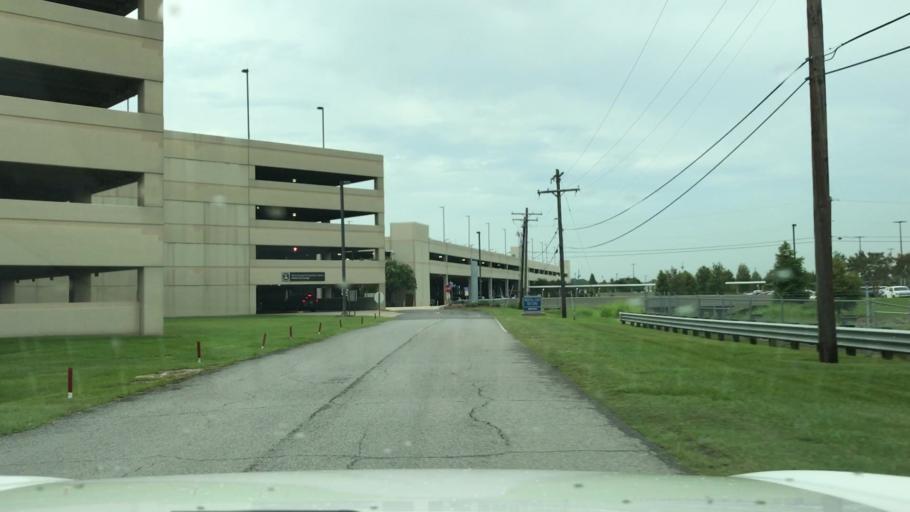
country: US
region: Louisiana
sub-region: East Baton Rouge Parish
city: Brownsfield
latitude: 30.5351
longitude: -91.1585
